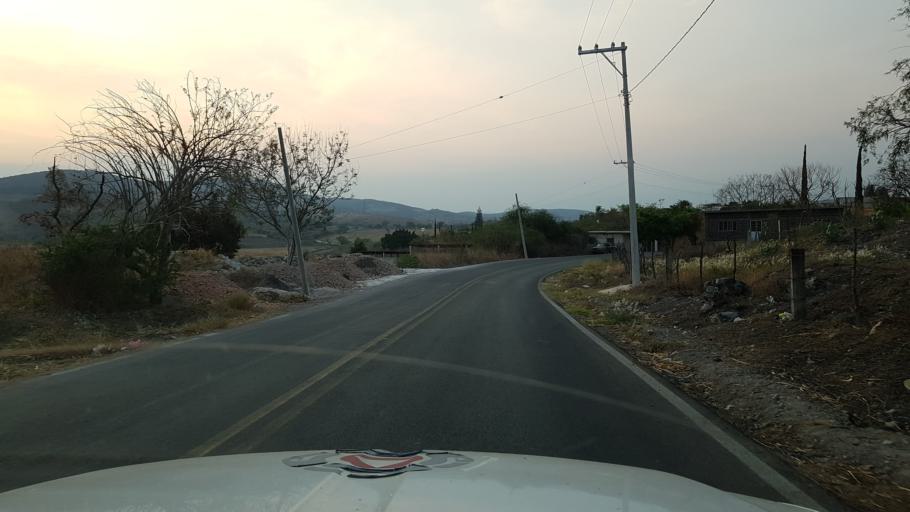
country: MX
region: Morelos
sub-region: Ayala
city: Abelardo L. Rodriguez
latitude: 18.7282
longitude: -99.0024
